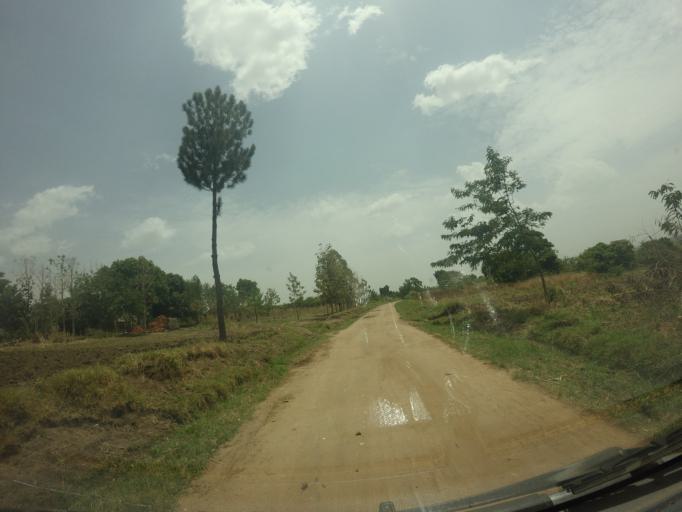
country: UG
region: Northern Region
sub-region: Arua District
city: Arua
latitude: 2.9397
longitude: 30.9152
